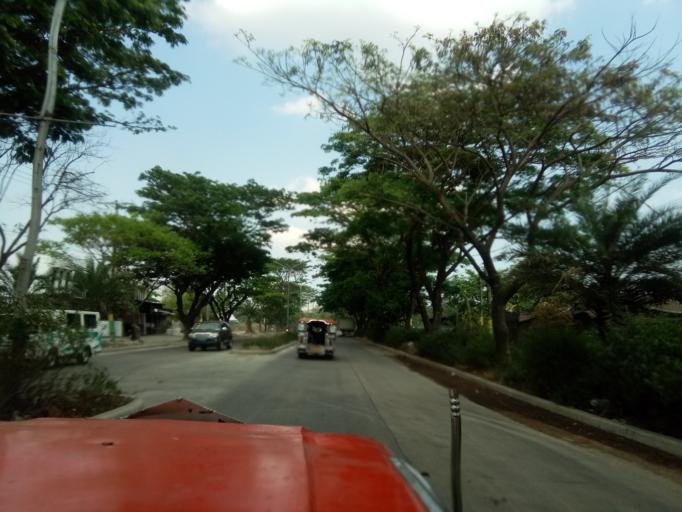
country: PH
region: Calabarzon
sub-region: Province of Cavite
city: Dasmarinas
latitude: 14.3275
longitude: 120.9532
